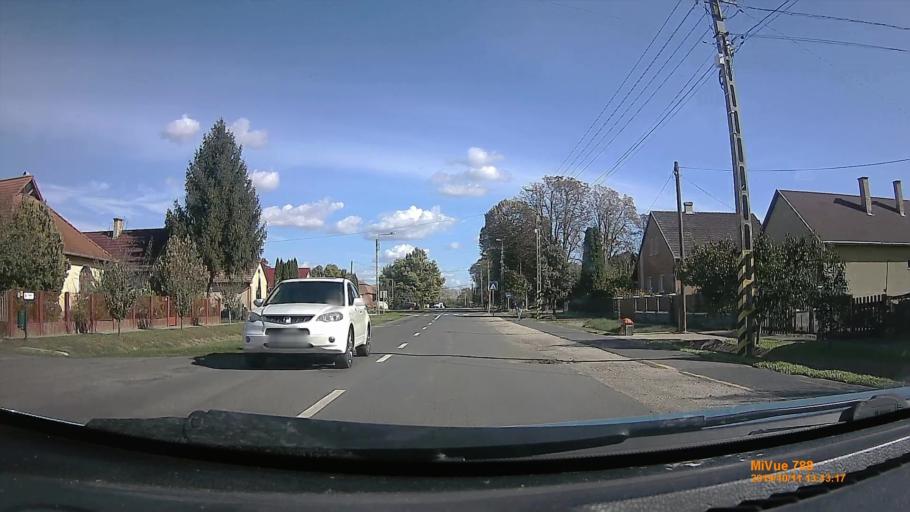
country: HU
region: Hajdu-Bihar
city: Balmazujvaros
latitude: 47.5389
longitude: 21.3505
